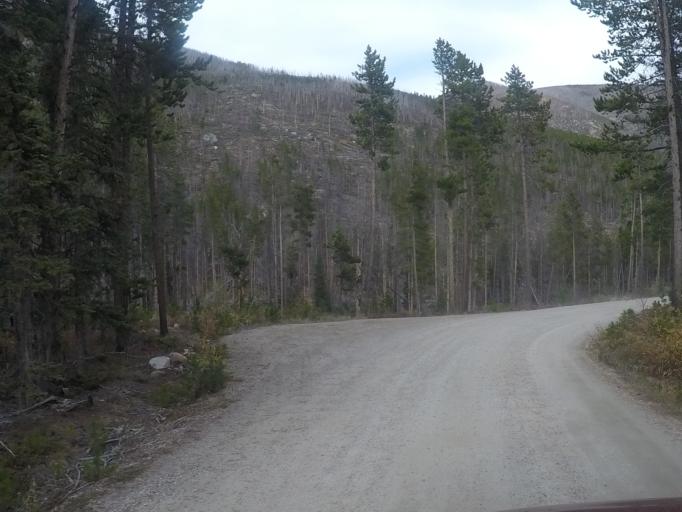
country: US
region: Montana
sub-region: Carbon County
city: Red Lodge
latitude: 45.1697
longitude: -109.4133
